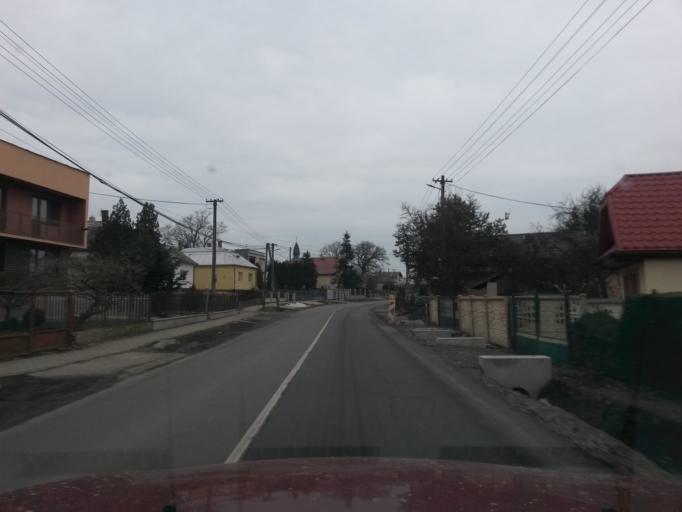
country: SK
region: Kosicky
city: Trebisov
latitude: 48.6857
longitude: 21.8120
